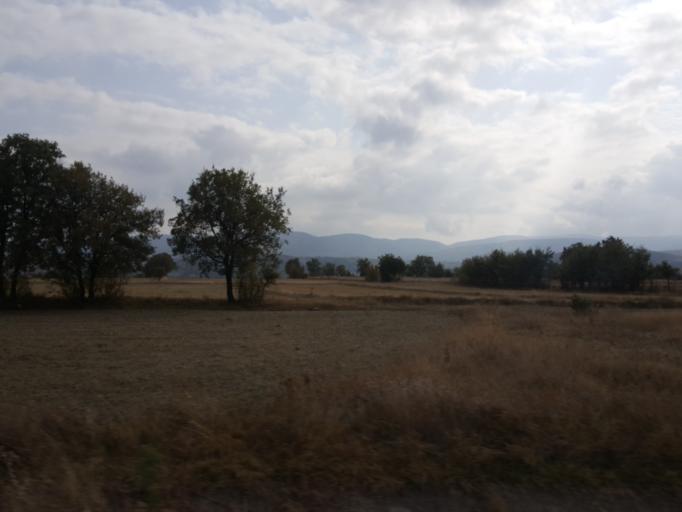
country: TR
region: Sinop
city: Sarayduzu
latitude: 41.3310
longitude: 34.7732
